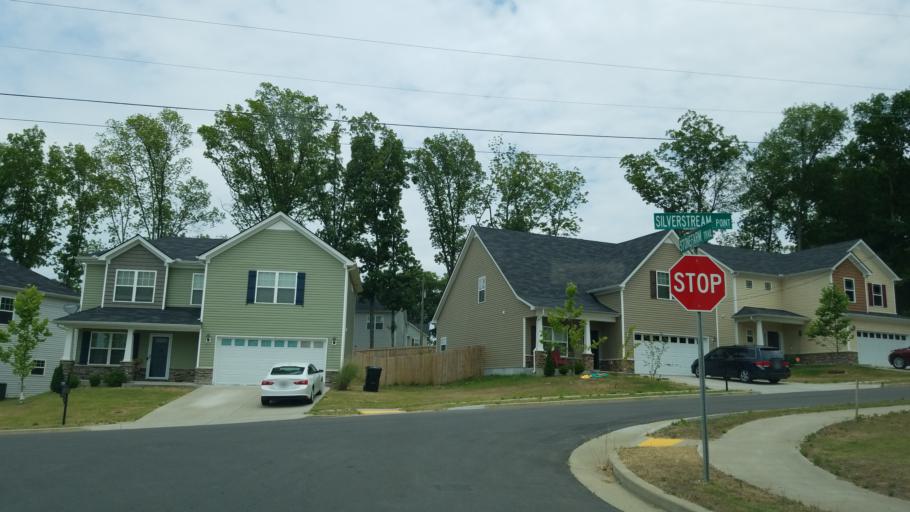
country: US
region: Tennessee
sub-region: Rutherford County
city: La Vergne
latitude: 36.0516
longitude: -86.6041
